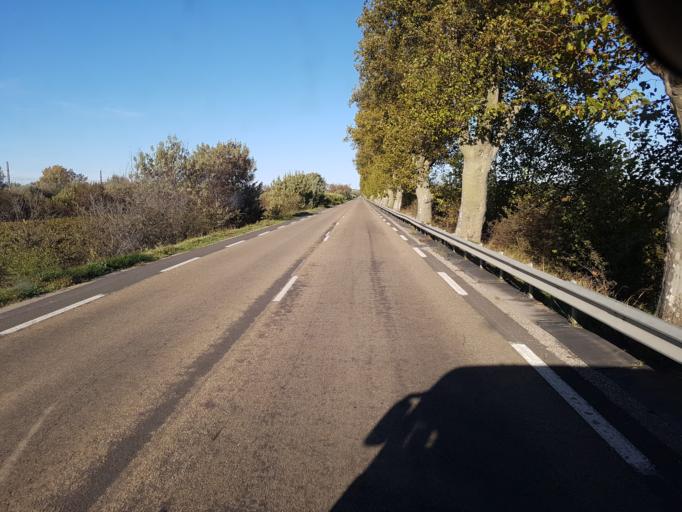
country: FR
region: Languedoc-Roussillon
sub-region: Departement de l'Aude
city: Coursan
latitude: 43.2455
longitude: 3.0648
